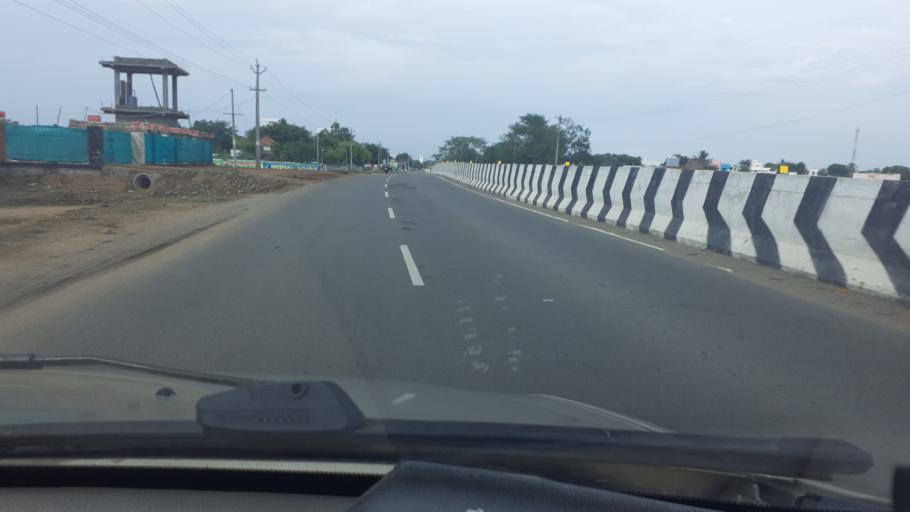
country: IN
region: Tamil Nadu
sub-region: Tirunelveli Kattabo
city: Tirunelveli
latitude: 8.6624
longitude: 77.7153
